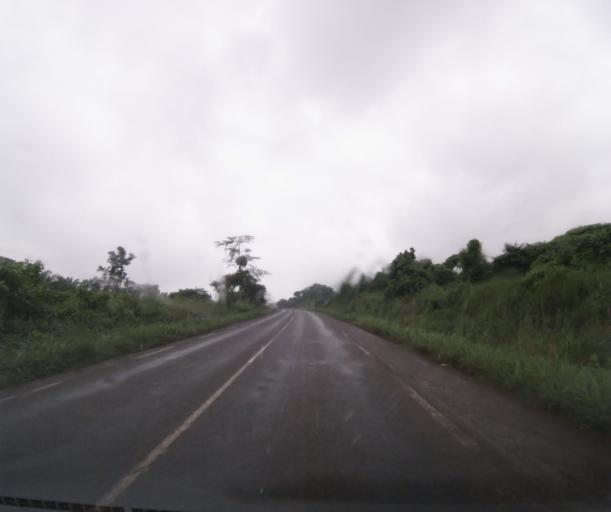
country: CM
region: Centre
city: Eseka
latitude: 3.8920
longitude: 10.7787
